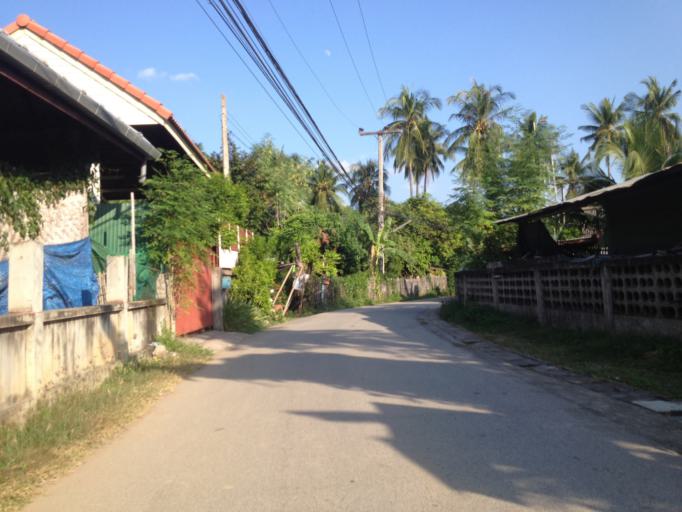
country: TH
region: Chiang Mai
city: Hang Dong
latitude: 18.7248
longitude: 98.9445
